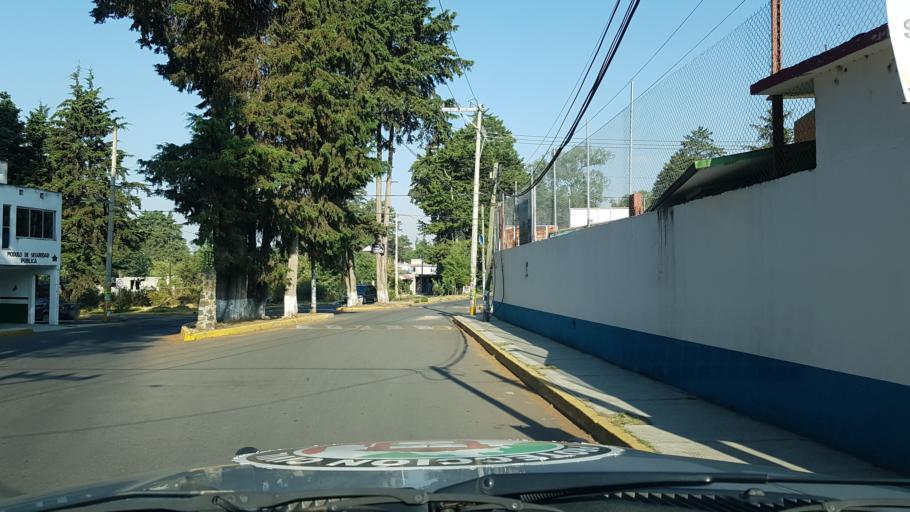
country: MX
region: Mexico
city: Ozumba de Alzate
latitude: 19.0617
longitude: -98.7813
